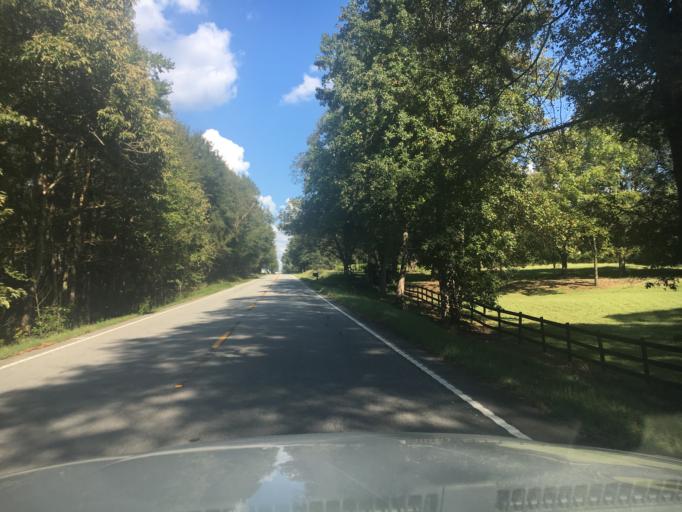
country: US
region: South Carolina
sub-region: Greenwood County
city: Ware Shoals
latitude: 34.5079
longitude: -82.2177
